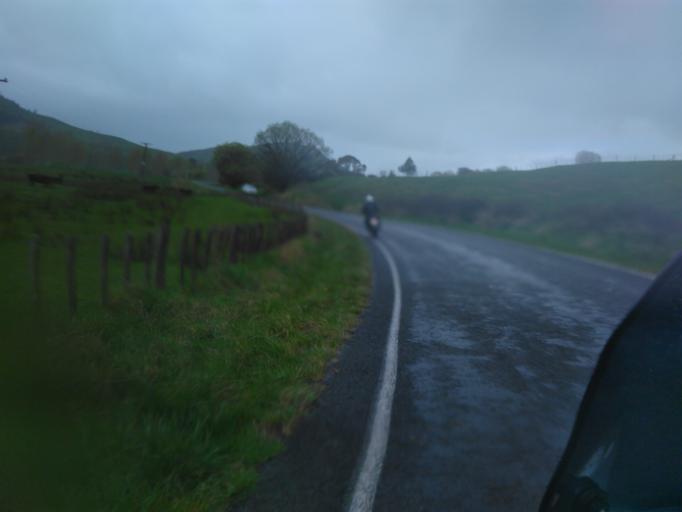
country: NZ
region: Gisborne
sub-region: Gisborne District
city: Gisborne
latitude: -38.6762
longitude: 177.7217
